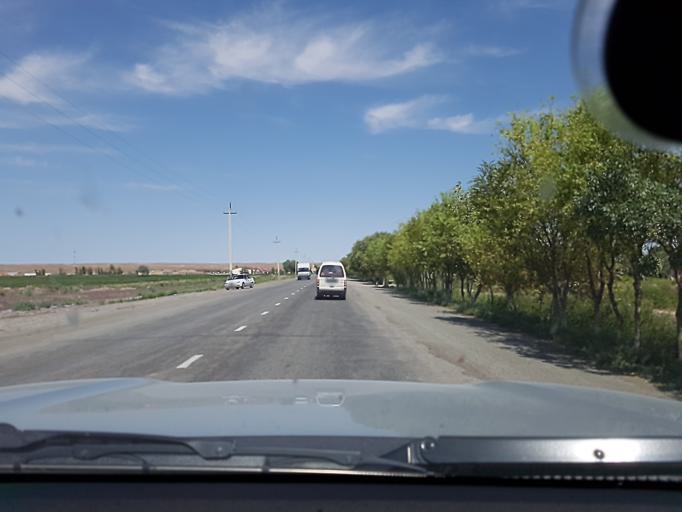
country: UZ
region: Karakalpakstan
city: Mang'it Shahri
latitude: 42.2392
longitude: 60.1440
